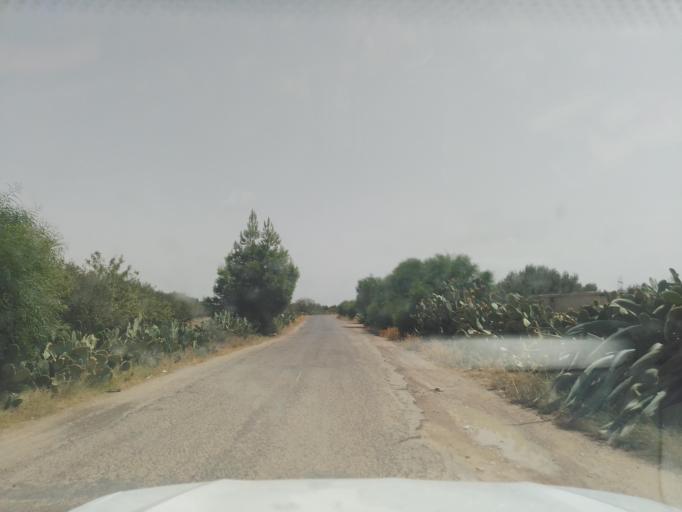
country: TN
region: Al Qasrayn
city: Kasserine
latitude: 35.2678
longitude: 9.0026
